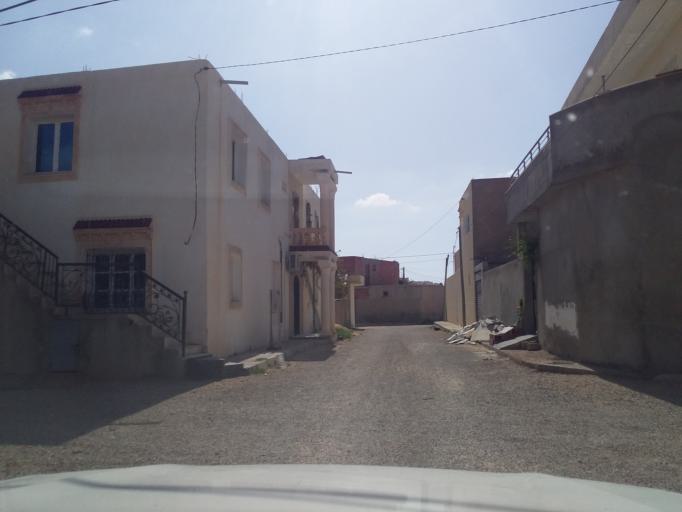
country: TN
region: Madanin
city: Medenine
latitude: 33.5825
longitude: 10.3219
